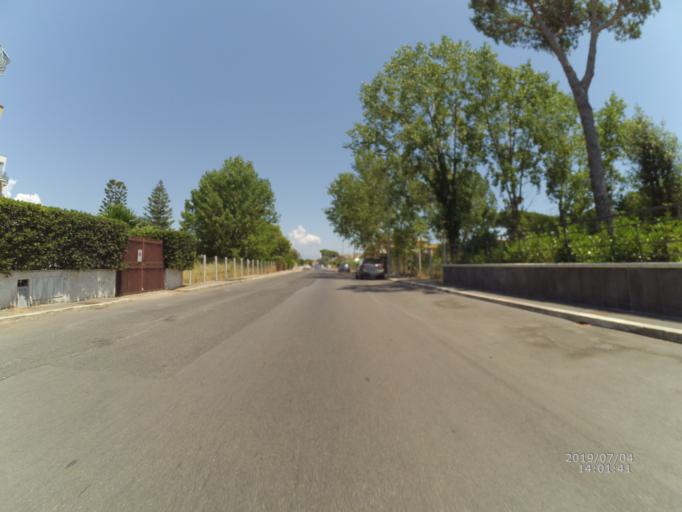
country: IT
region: Latium
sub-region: Provincia di Latina
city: Terracina
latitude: 41.2862
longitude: 13.2283
